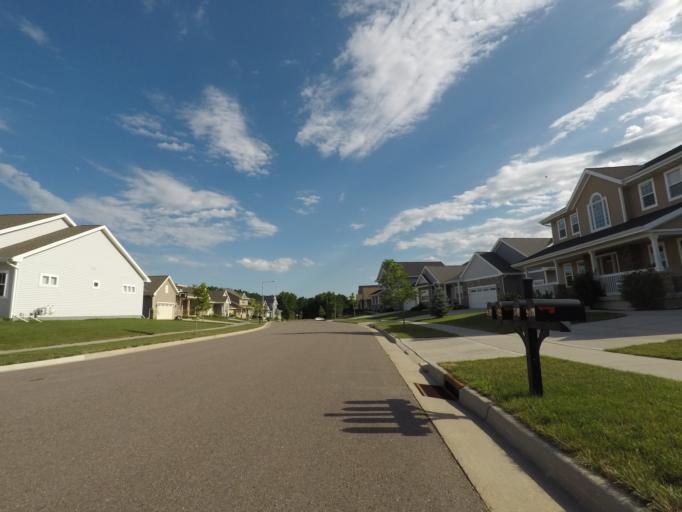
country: US
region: Wisconsin
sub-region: Dane County
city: Middleton
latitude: 43.0689
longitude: -89.5600
